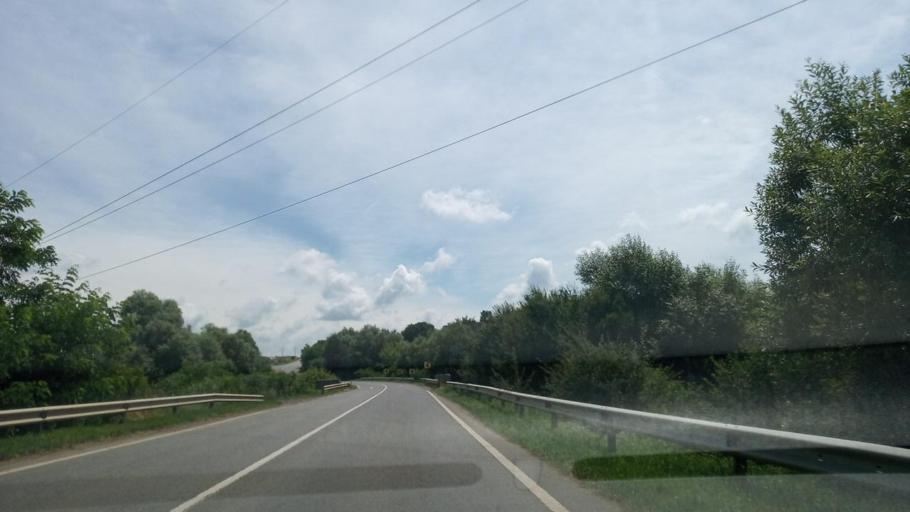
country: RO
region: Alba
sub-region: Comuna Cut
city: Cut
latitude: 45.9199
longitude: 23.6936
